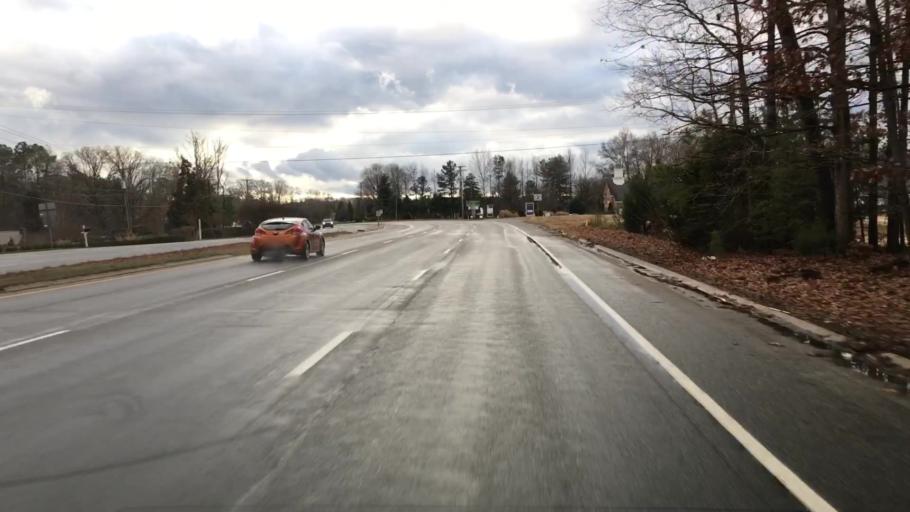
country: US
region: Virginia
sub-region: Chesterfield County
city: Bon Air
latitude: 37.4838
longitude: -77.5981
